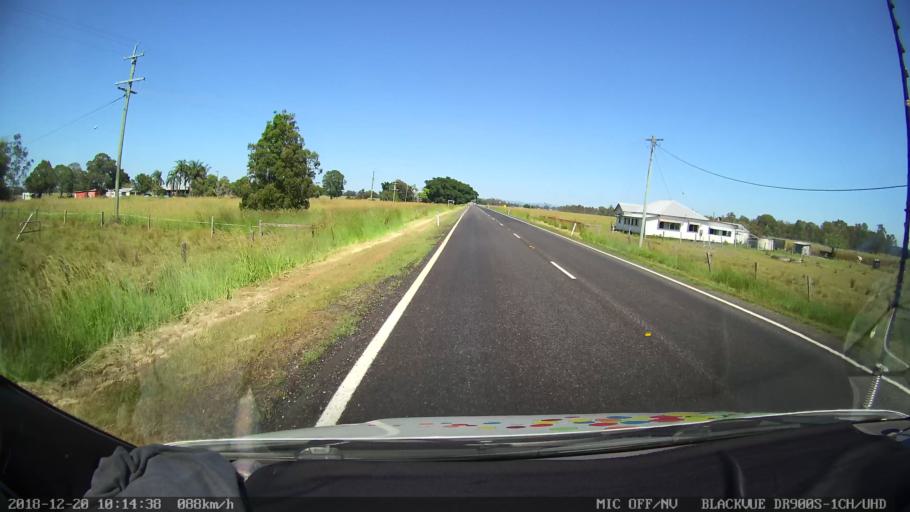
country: AU
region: New South Wales
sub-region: Richmond Valley
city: Casino
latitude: -28.8696
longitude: 153.1119
